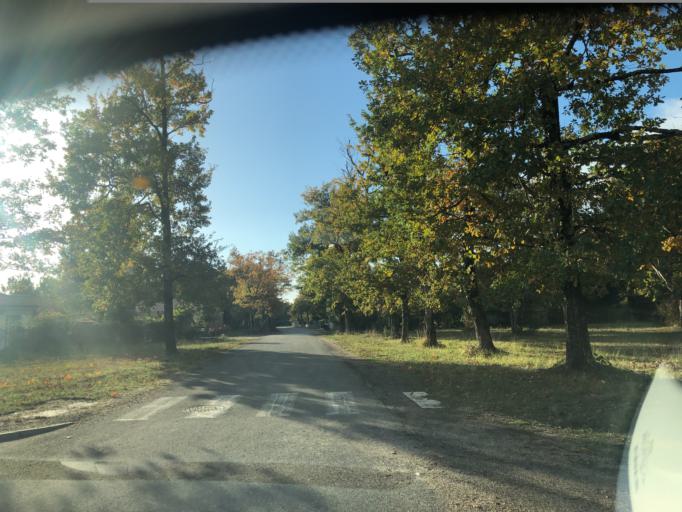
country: FR
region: Aquitaine
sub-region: Departement de la Gironde
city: Hourtin
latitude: 45.1838
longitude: -1.0490
